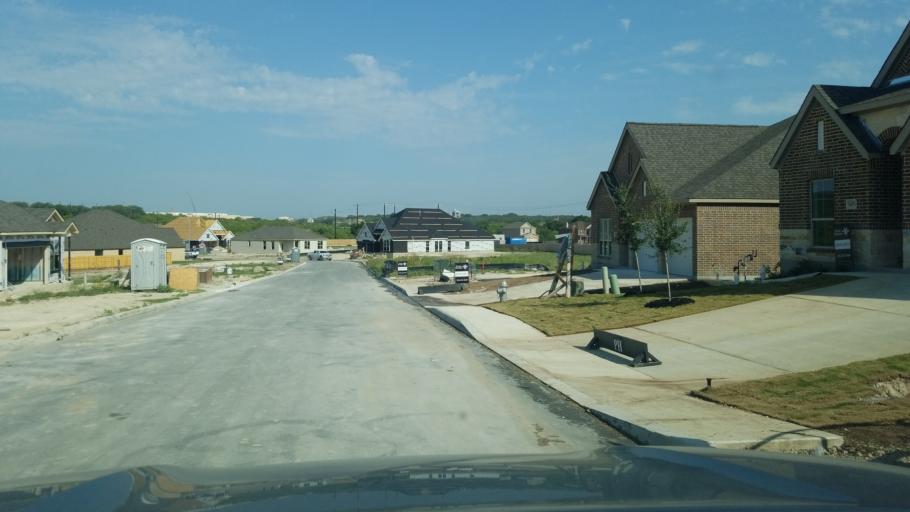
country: US
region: Texas
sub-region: Medina County
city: La Coste
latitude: 29.4075
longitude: -98.7862
